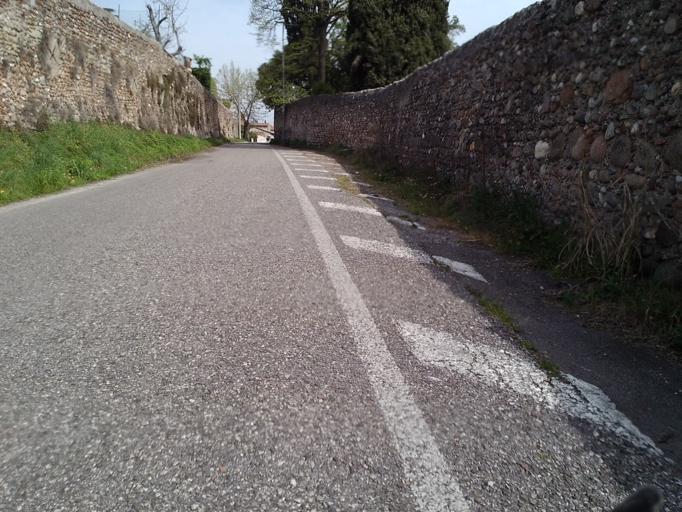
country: IT
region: Veneto
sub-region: Provincia di Verona
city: Sommacampagna
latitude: 45.4047
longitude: 10.8414
